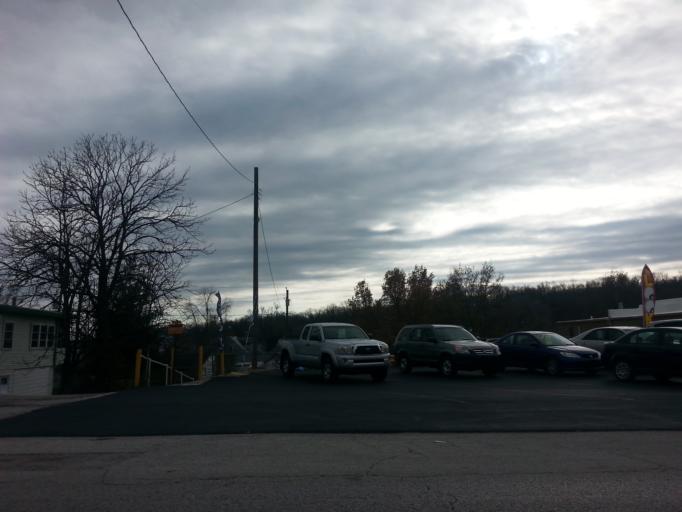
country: US
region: Missouri
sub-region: Marion County
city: Hannibal
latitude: 39.7035
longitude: -91.3804
